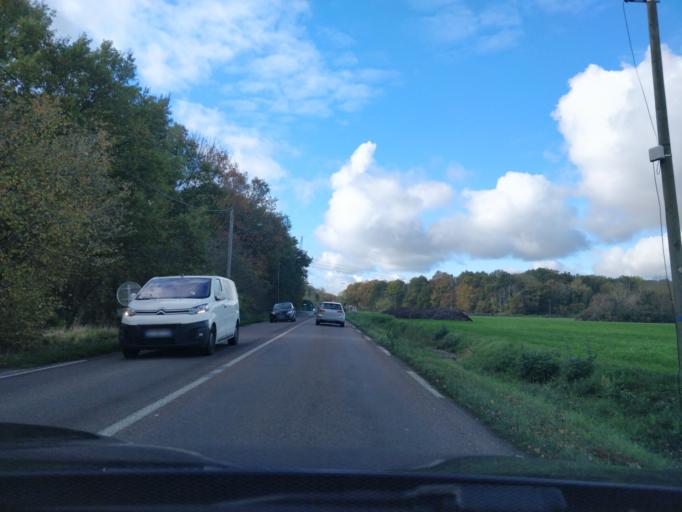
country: FR
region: Ile-de-France
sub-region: Departement de l'Essonne
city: Ollainville
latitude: 48.6024
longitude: 2.2187
